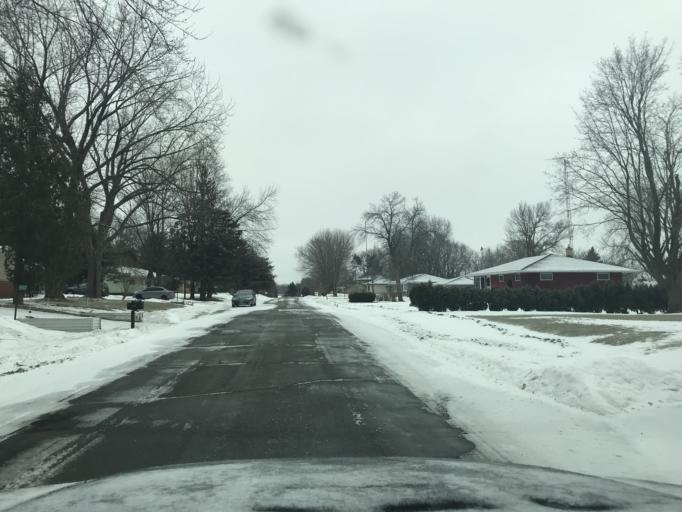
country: US
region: Wisconsin
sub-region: Dane County
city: Cottage Grove
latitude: 43.0975
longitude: -89.2369
